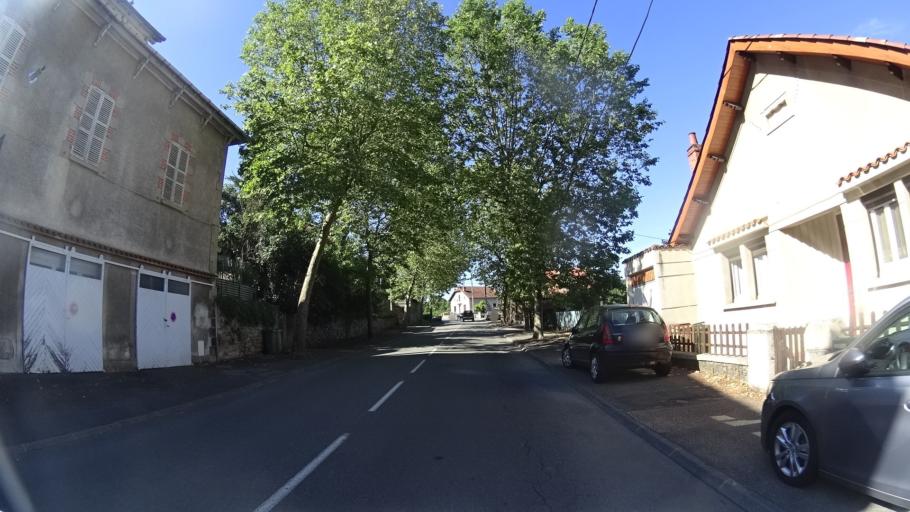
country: FR
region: Midi-Pyrenees
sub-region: Departement du Lot
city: Figeac
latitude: 44.6123
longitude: 2.0282
